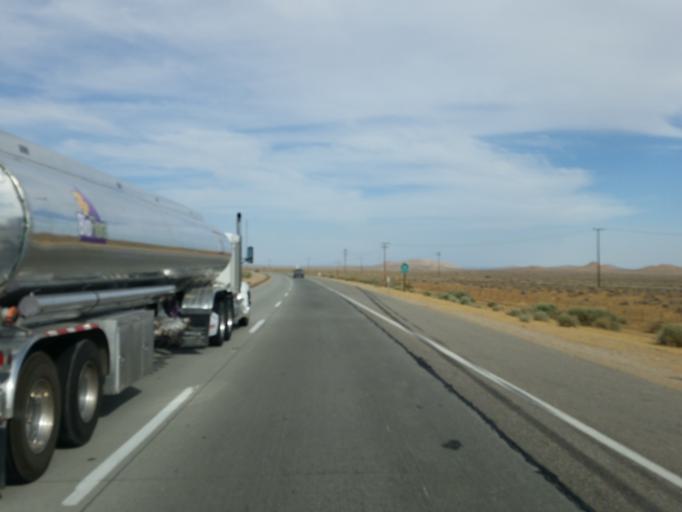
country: US
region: California
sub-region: Kern County
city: Mojave
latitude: 35.0329
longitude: -118.1005
